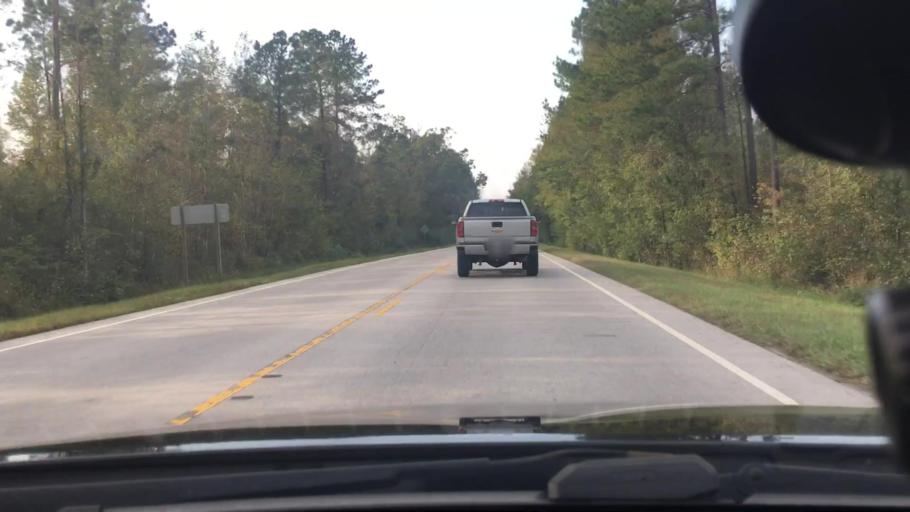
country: US
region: North Carolina
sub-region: Craven County
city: Vanceboro
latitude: 35.3108
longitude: -77.1388
